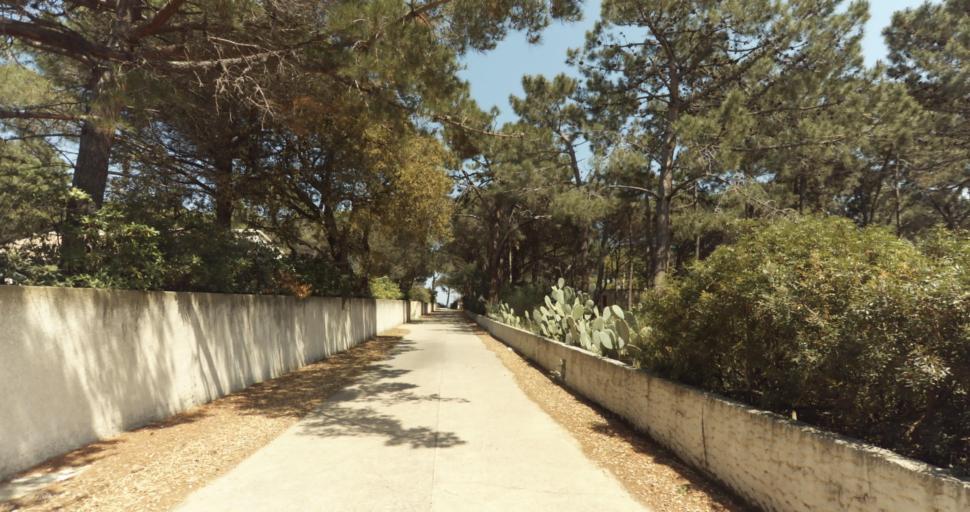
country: FR
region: Corsica
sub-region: Departement de la Haute-Corse
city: Biguglia
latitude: 42.6334
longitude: 9.4640
